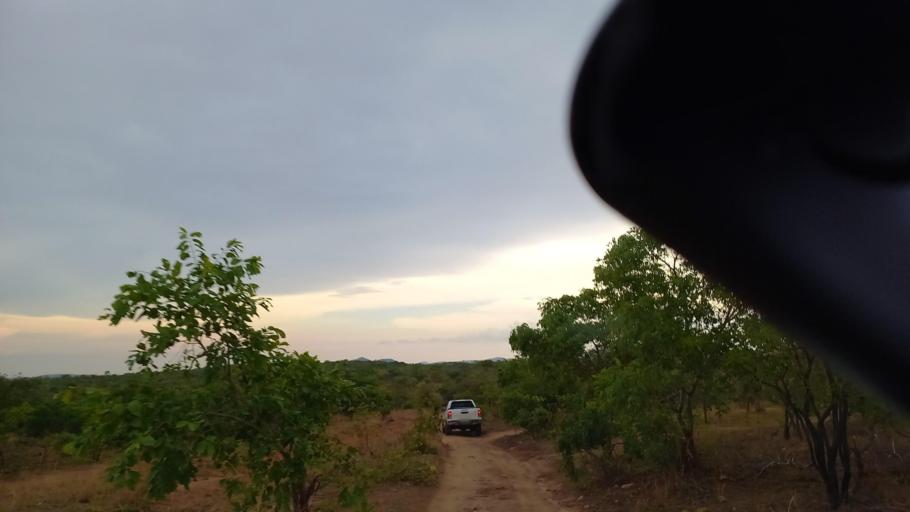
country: ZM
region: Lusaka
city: Kafue
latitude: -16.0473
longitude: 28.3211
